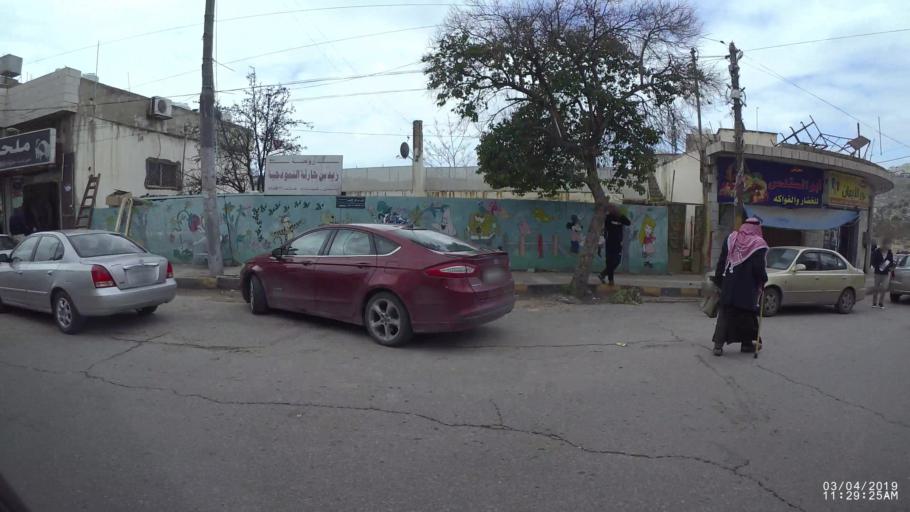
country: JO
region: Amman
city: Wadi as Sir
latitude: 31.9529
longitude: 35.8202
